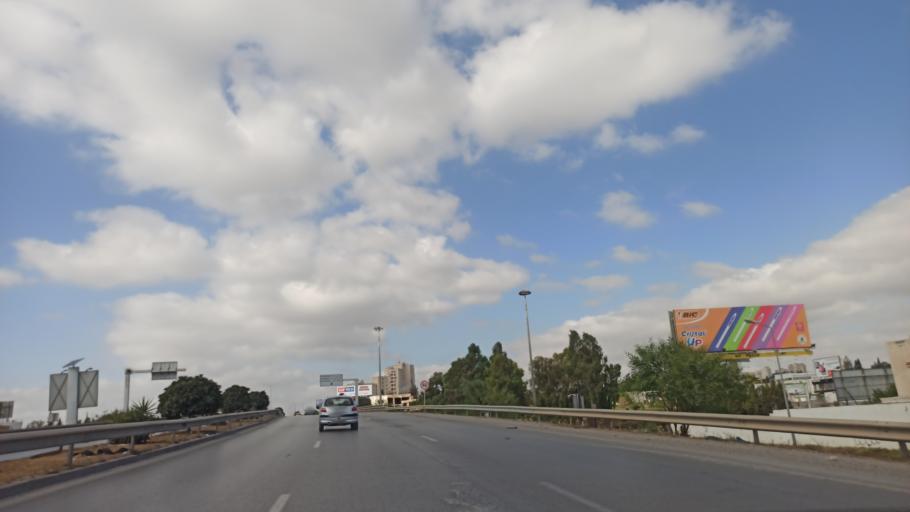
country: TN
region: Ariana
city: Ariana
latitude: 36.8486
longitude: 10.1845
